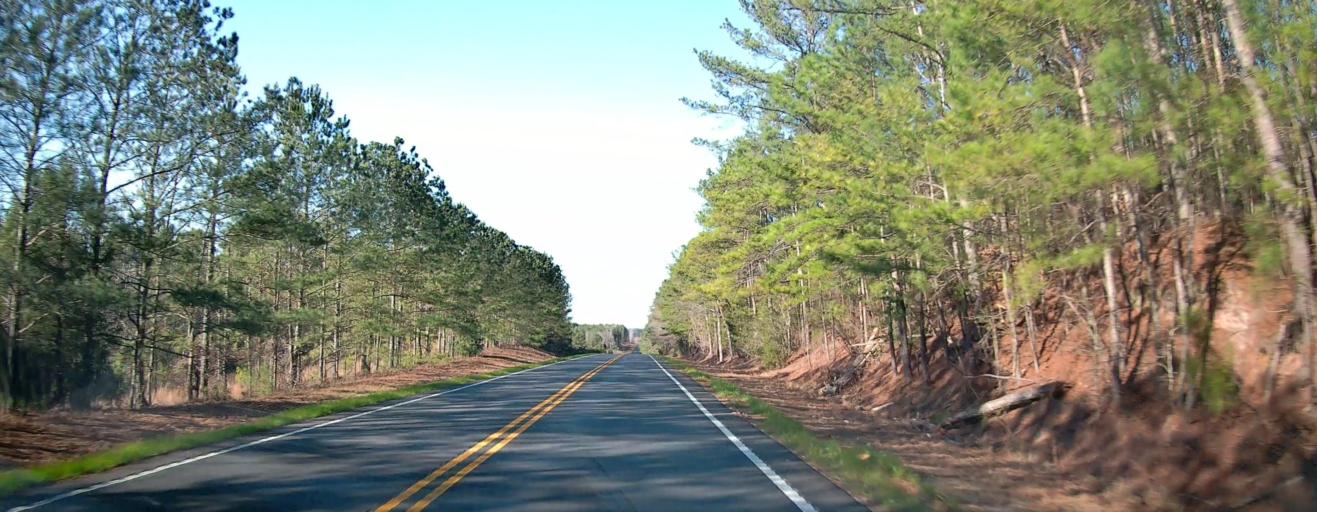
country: US
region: Georgia
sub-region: Talbot County
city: Sardis
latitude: 32.7826
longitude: -84.6926
